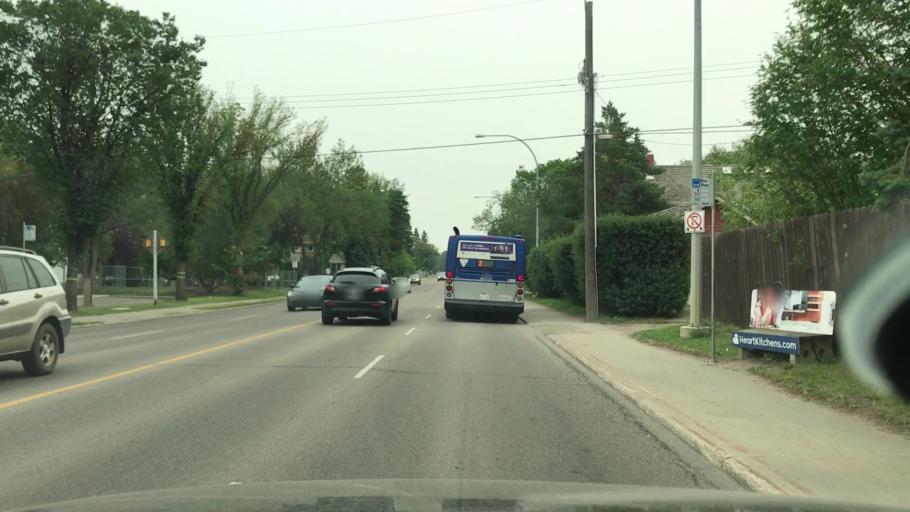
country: CA
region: Alberta
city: Edmonton
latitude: 53.5458
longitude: -113.5525
